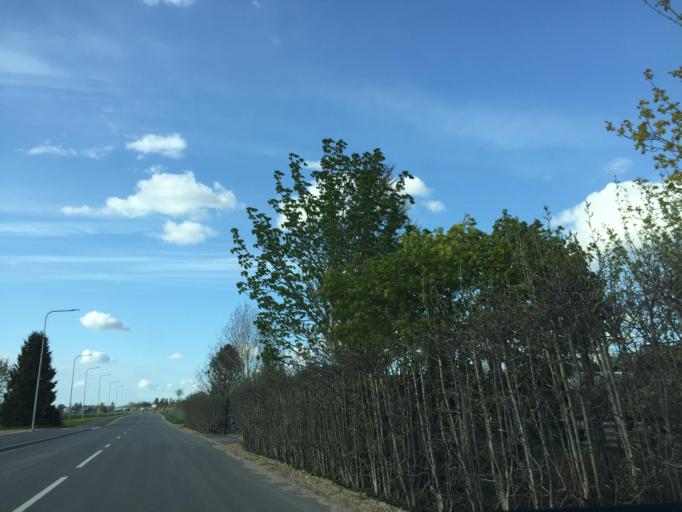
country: LV
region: Sigulda
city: Sigulda
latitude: 57.1333
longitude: 24.8620
